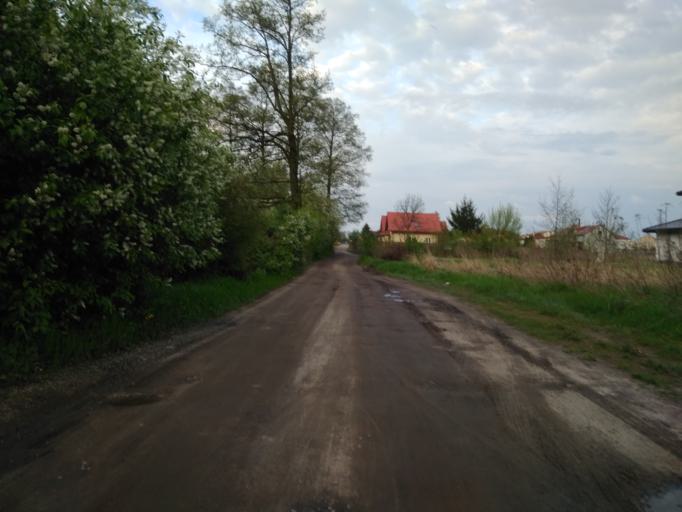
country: PL
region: Masovian Voivodeship
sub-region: Warszawa
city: Targowek
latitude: 52.3283
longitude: 21.0415
